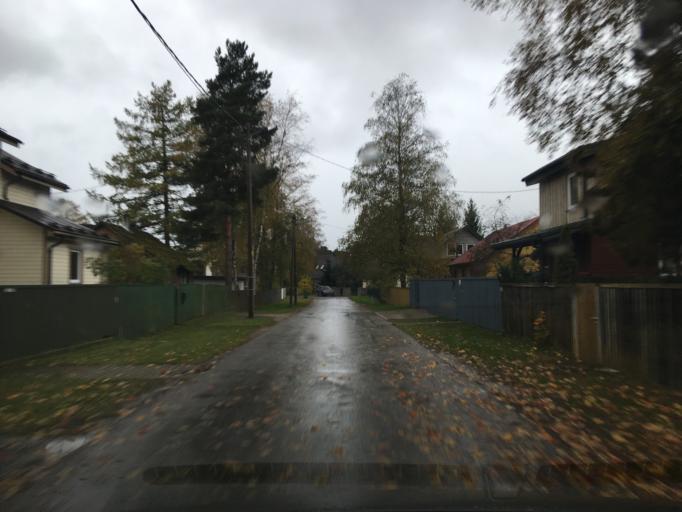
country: EE
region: Harju
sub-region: Saue vald
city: Laagri
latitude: 59.3666
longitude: 24.6384
